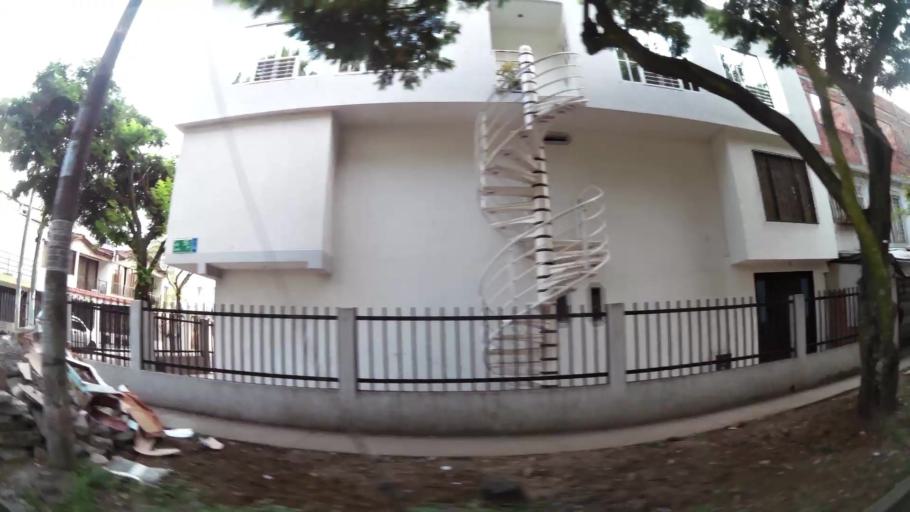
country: CO
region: Valle del Cauca
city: Cali
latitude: 3.4714
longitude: -76.4965
